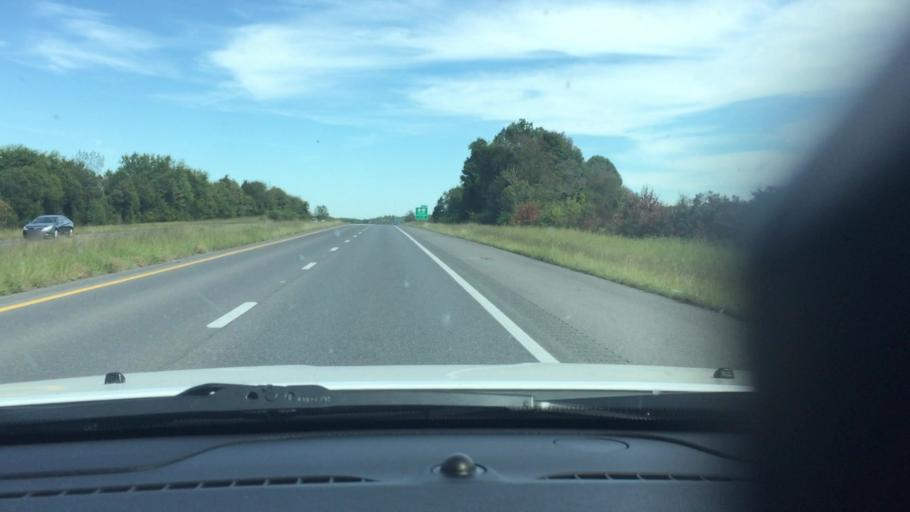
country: US
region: Kentucky
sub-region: Caldwell County
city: Princeton
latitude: 37.1186
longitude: -87.9122
